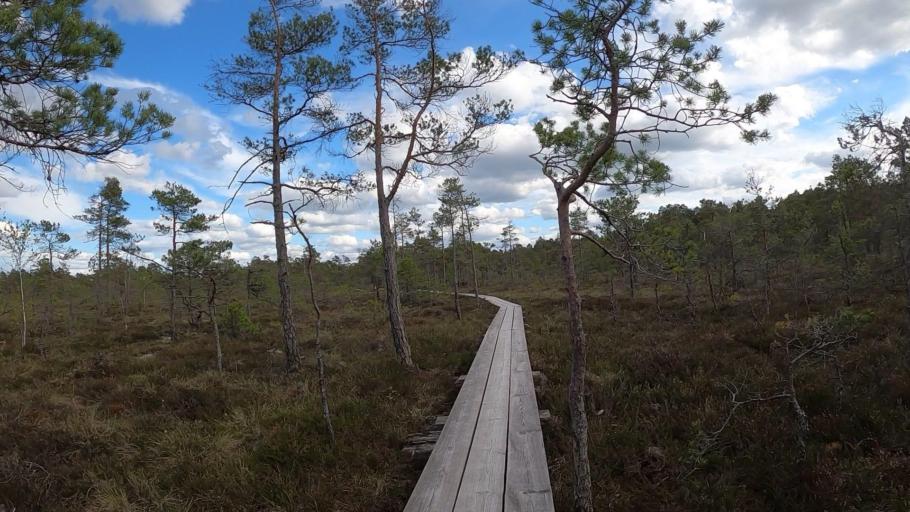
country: LV
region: Jurmala
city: Jurmala
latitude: 56.8557
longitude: 23.8101
